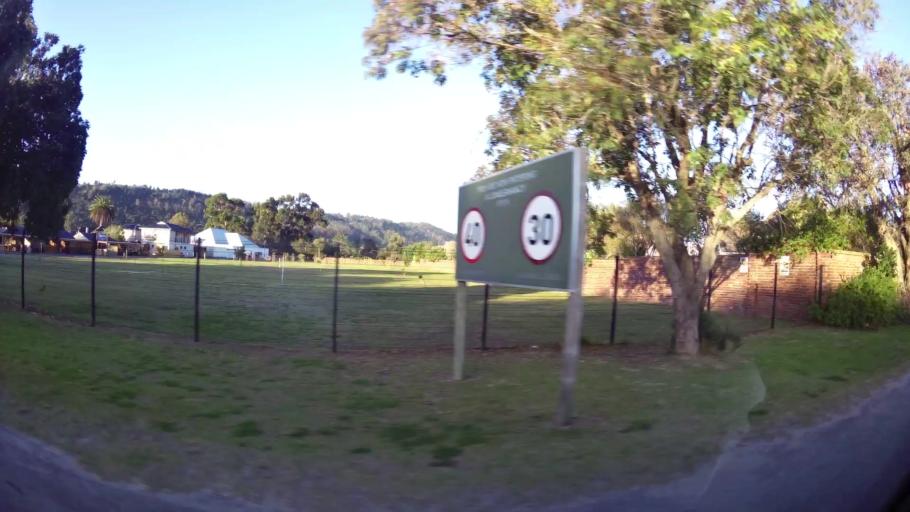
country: ZA
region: Western Cape
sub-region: Eden District Municipality
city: Knysna
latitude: -34.0111
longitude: 22.7791
